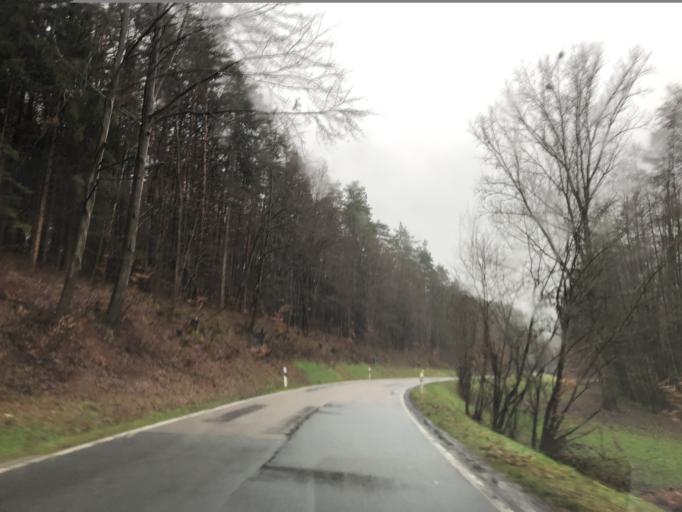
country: DE
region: Hesse
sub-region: Regierungsbezirk Darmstadt
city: Lutzelbach
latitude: 49.7795
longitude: 9.1125
